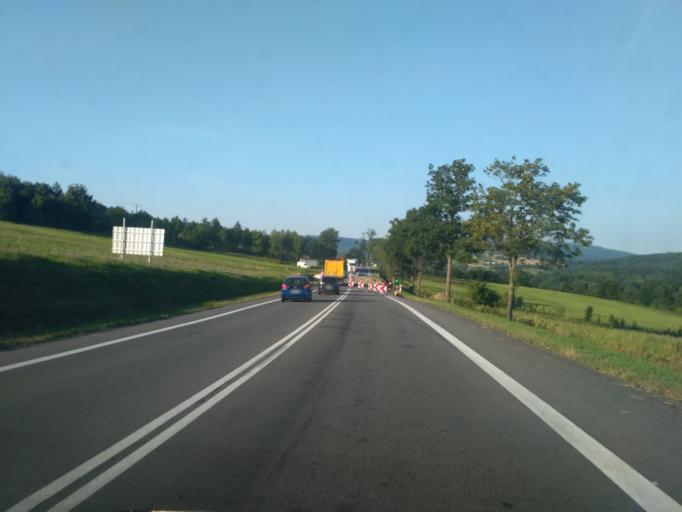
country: PL
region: Subcarpathian Voivodeship
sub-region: Powiat krosnienski
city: Dukla
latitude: 49.5865
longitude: 21.7061
